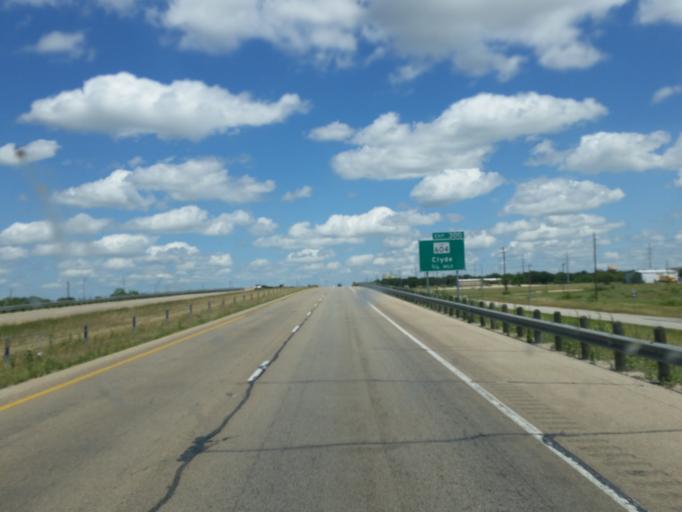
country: US
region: Texas
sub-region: Callahan County
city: Clyde
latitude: 32.4186
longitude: -99.5283
